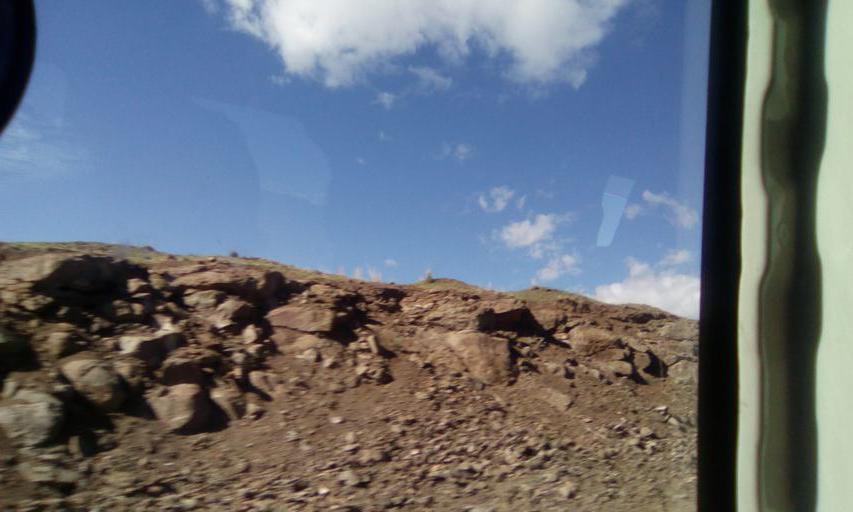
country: LS
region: Qacha's Nek
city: Qacha's Nek
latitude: -30.0430
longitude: 28.2425
